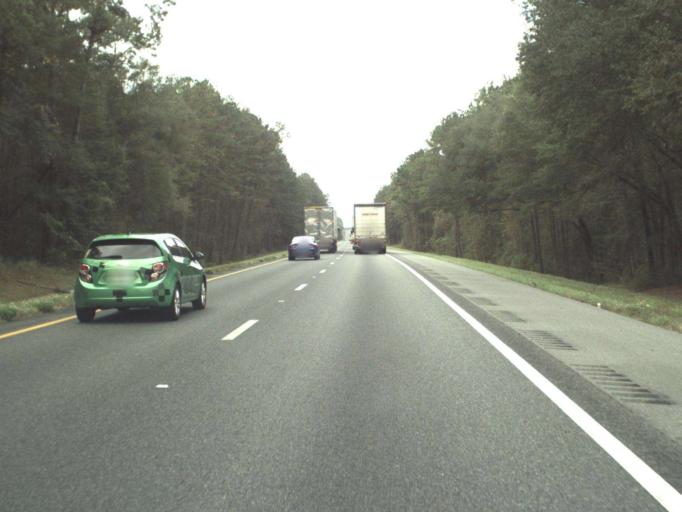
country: US
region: Florida
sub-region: Gadsden County
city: Midway
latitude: 30.5128
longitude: -84.4721
